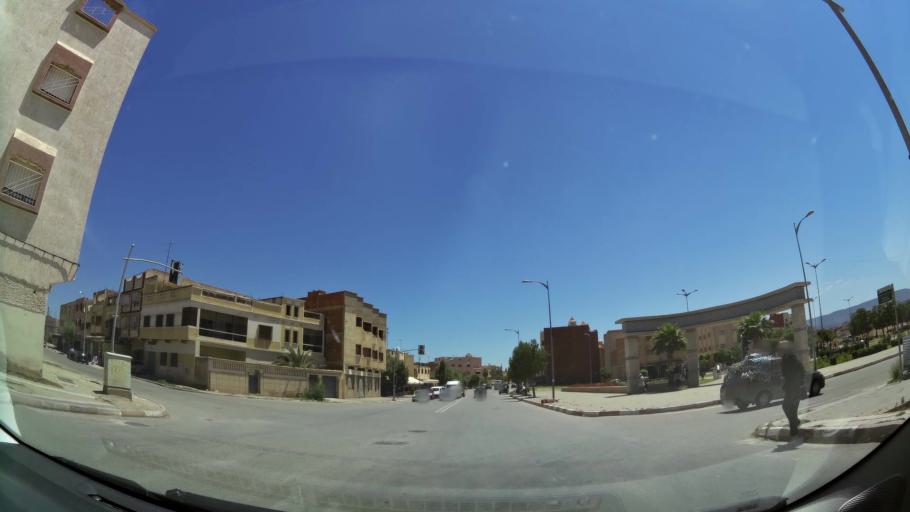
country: MA
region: Oriental
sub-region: Oujda-Angad
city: Oujda
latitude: 34.6764
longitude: -1.8827
